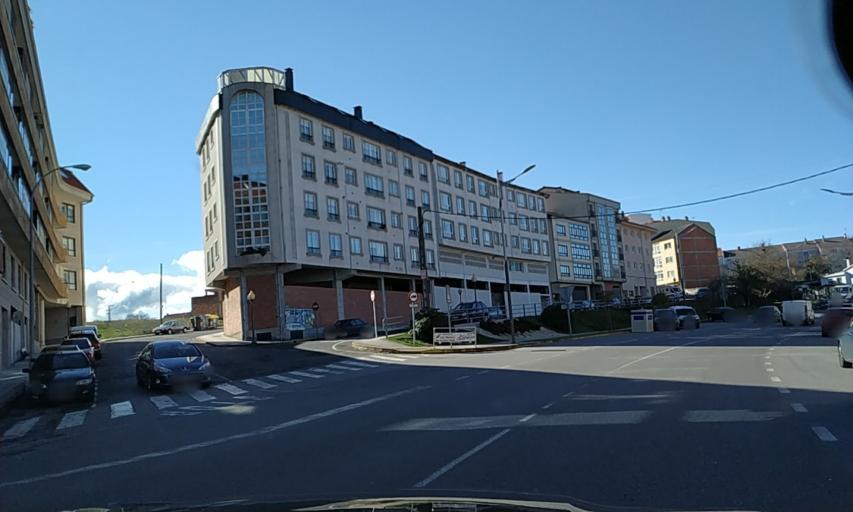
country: ES
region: Galicia
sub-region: Provincia de Pontevedra
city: Silleda
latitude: 42.6959
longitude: -8.2422
